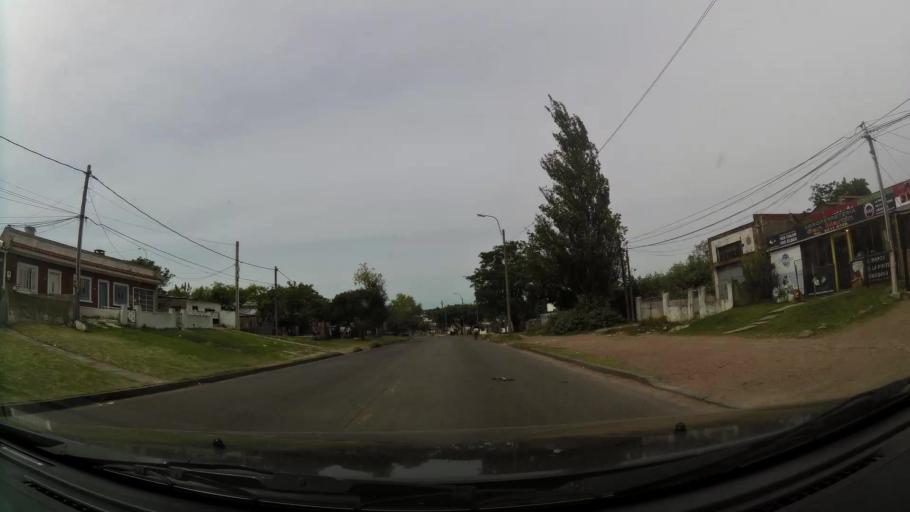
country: UY
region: Montevideo
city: Montevideo
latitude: -34.8415
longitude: -56.1691
